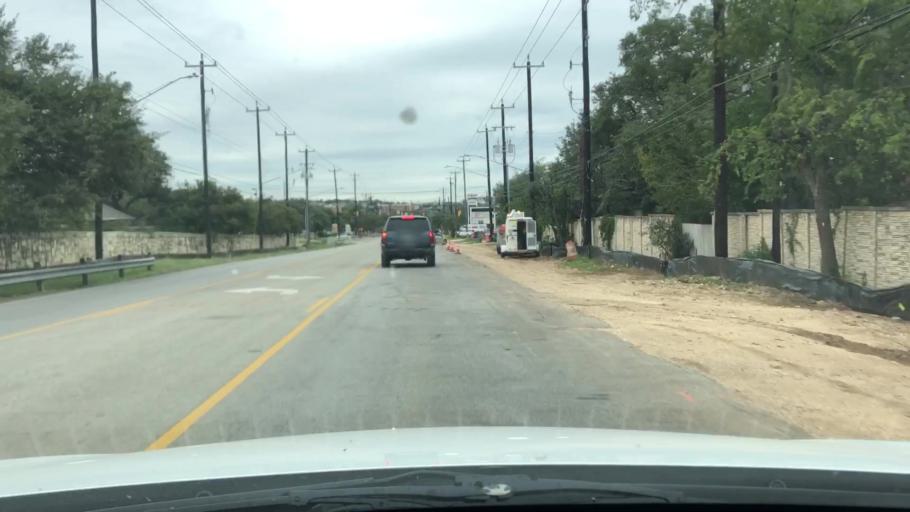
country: US
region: Texas
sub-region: Bexar County
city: Shavano Park
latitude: 29.5722
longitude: -98.5719
